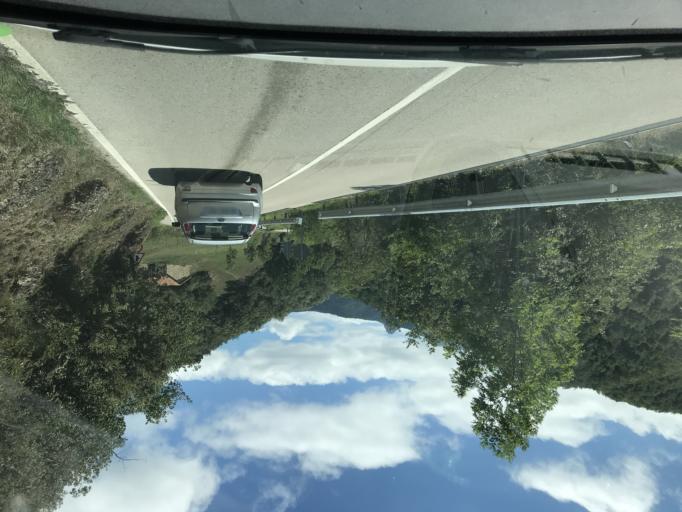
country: ES
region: Cantabria
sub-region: Provincia de Cantabria
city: Cabezon de Liebana
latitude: 43.0762
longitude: -4.5074
